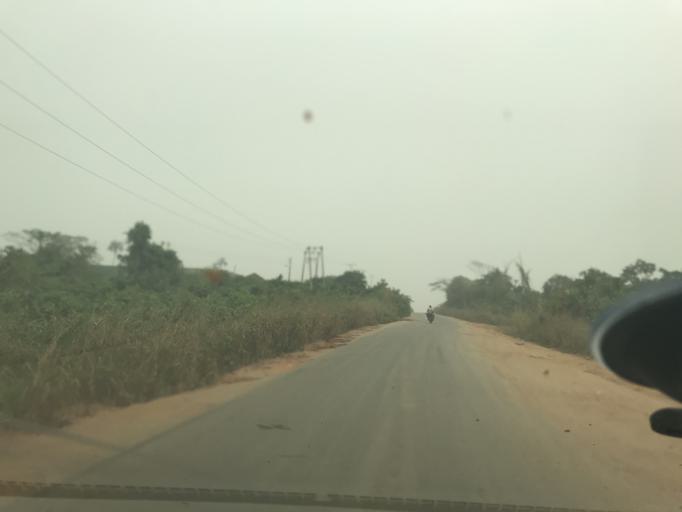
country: NG
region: Ogun
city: Owode
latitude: 6.8928
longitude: 3.5630
